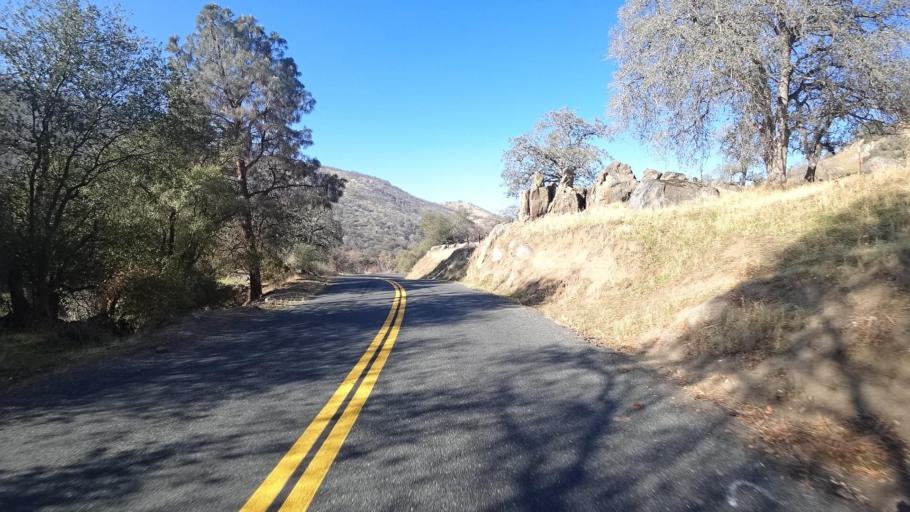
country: US
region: California
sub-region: Kern County
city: Alta Sierra
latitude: 35.7904
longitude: -118.7999
